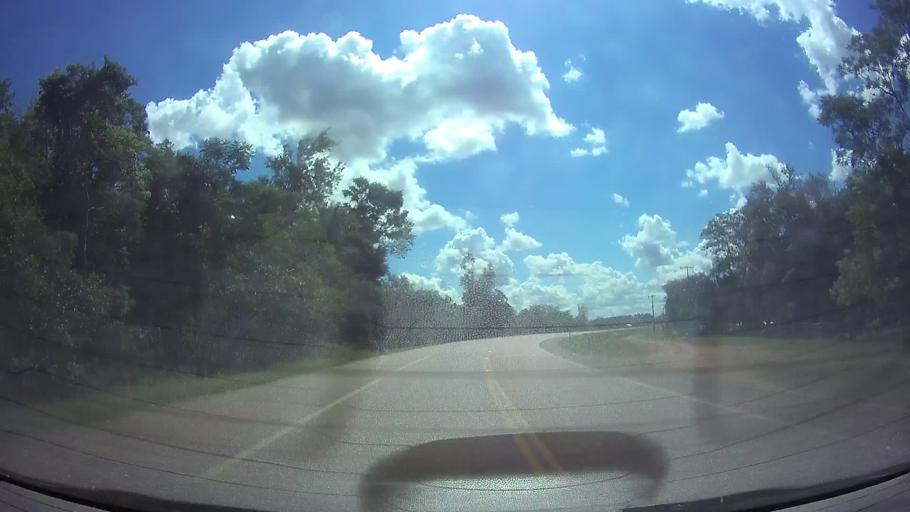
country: PY
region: Guaira
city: Itape
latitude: -25.9172
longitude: -56.7047
